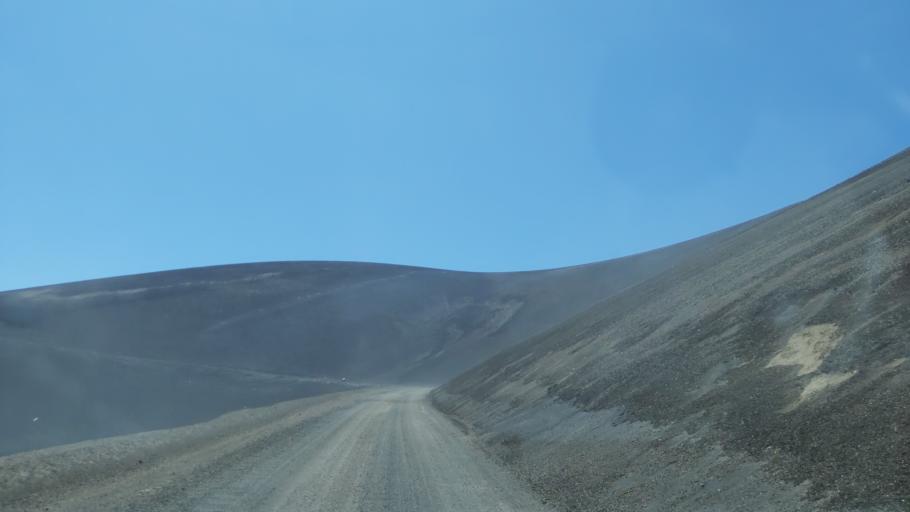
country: CL
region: Araucania
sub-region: Provincia de Cautin
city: Vilcun
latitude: -38.3916
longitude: -71.5454
